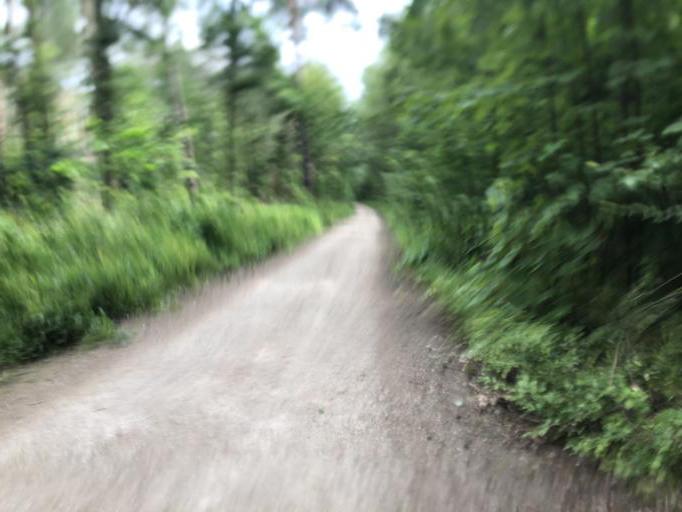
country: DE
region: Bavaria
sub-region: Regierungsbezirk Mittelfranken
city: Mohrendorf
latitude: 49.6095
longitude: 10.9668
